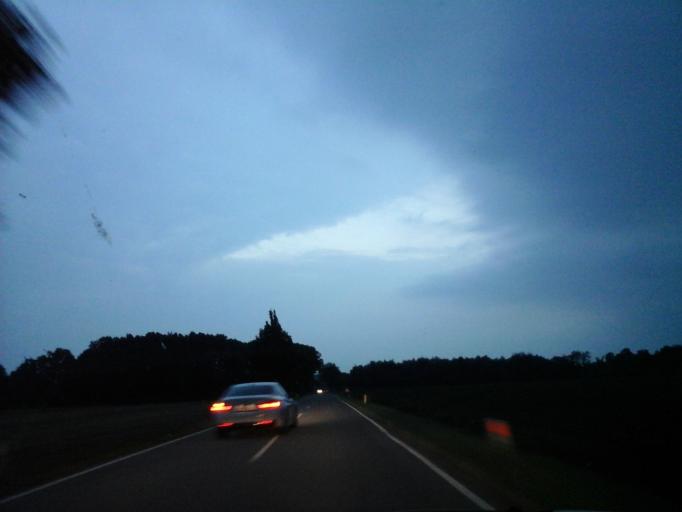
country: AT
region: Lower Austria
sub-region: Politischer Bezirk Ganserndorf
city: Angern an der March
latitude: 48.3166
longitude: 16.8480
